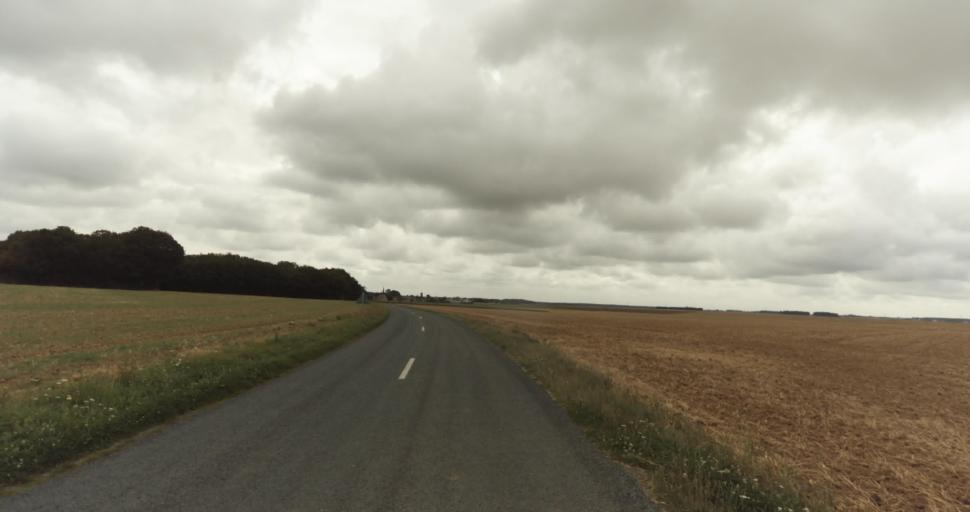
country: FR
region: Haute-Normandie
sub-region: Departement de l'Eure
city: La Couture-Boussey
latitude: 48.9381
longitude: 1.3831
